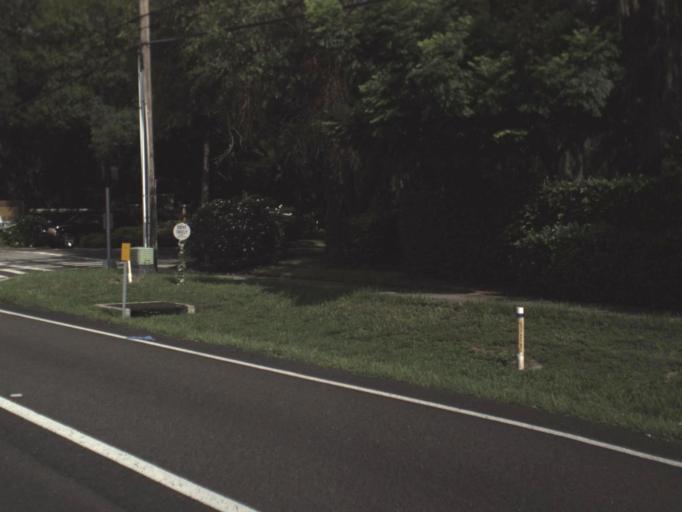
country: US
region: Florida
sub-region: Hillsborough County
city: Temple Terrace
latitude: 28.0545
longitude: -82.3854
